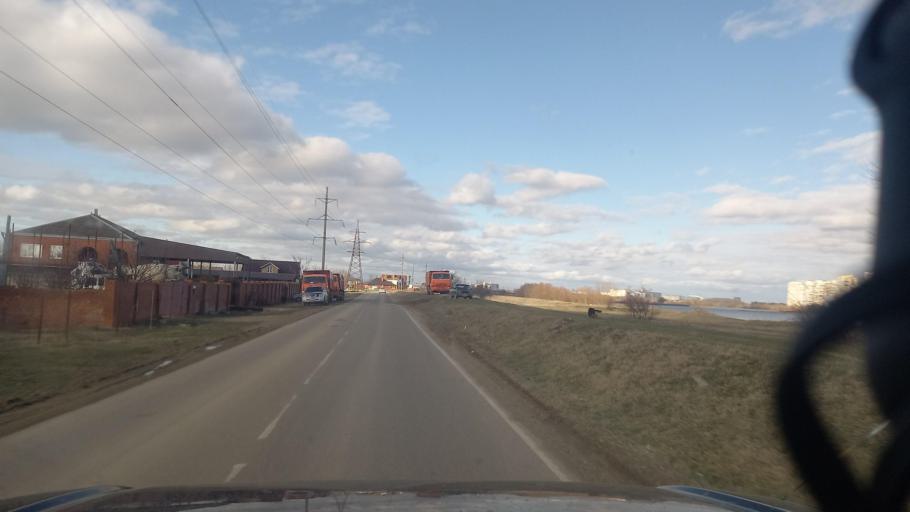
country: RU
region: Adygeya
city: Yablonovskiy
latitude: 45.0274
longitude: 38.8975
